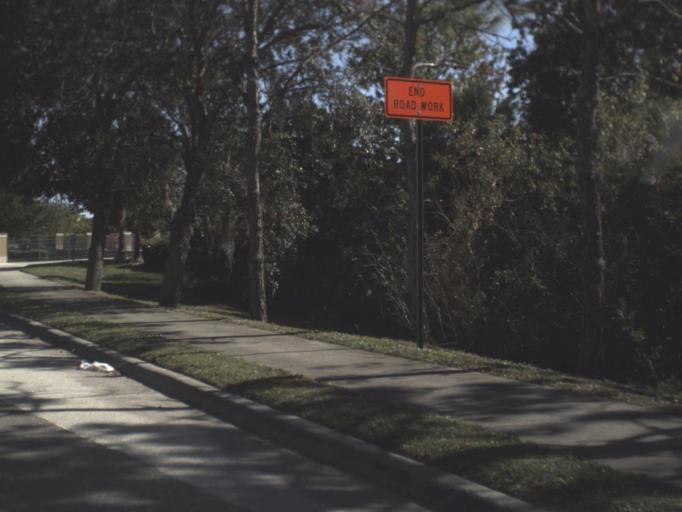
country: US
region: Florida
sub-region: Brevard County
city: South Patrick Shores
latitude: 28.2303
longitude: -80.7104
